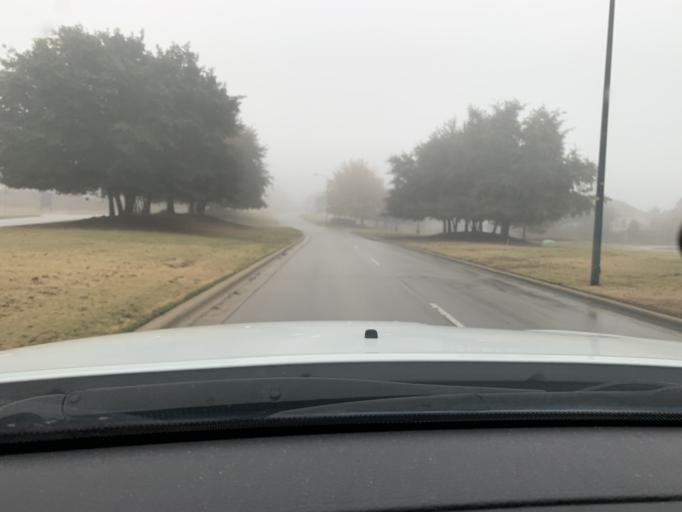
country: US
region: Texas
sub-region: Williamson County
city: Round Rock
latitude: 30.5699
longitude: -97.6711
